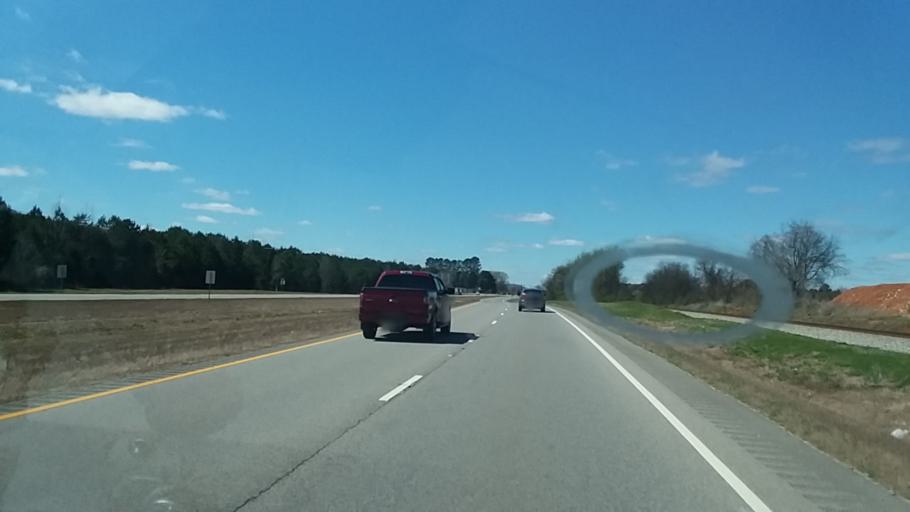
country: US
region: Alabama
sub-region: Colbert County
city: Tuscumbia
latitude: 34.7230
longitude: -87.8149
